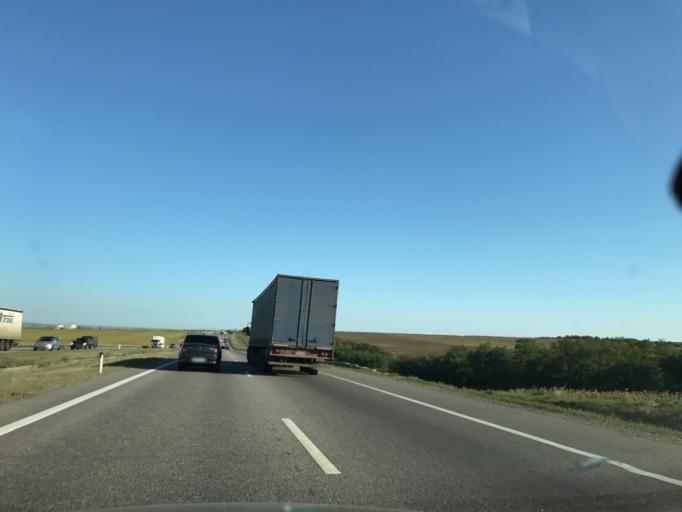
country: RU
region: Rostov
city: Glubokiy
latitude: 48.4655
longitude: 40.3409
